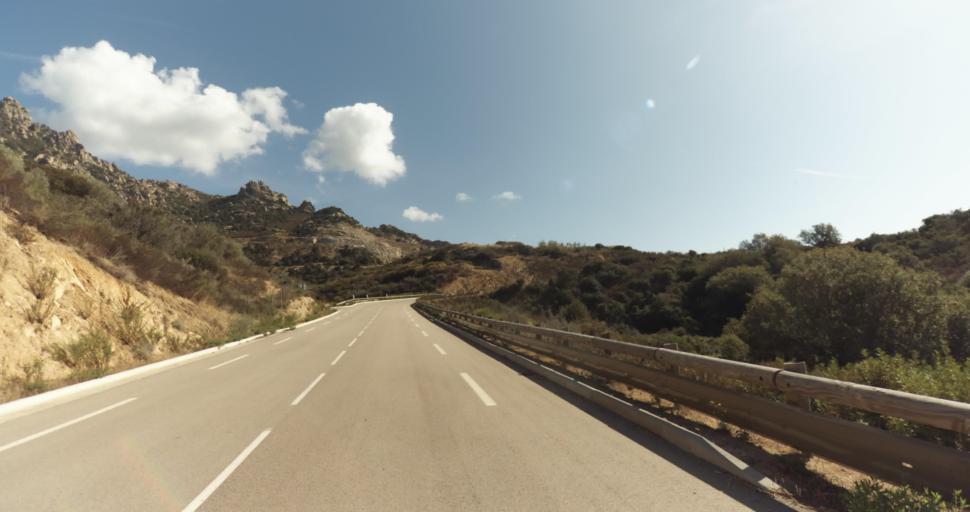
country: FR
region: Corsica
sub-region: Departement de la Corse-du-Sud
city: Ajaccio
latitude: 41.9328
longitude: 8.6702
